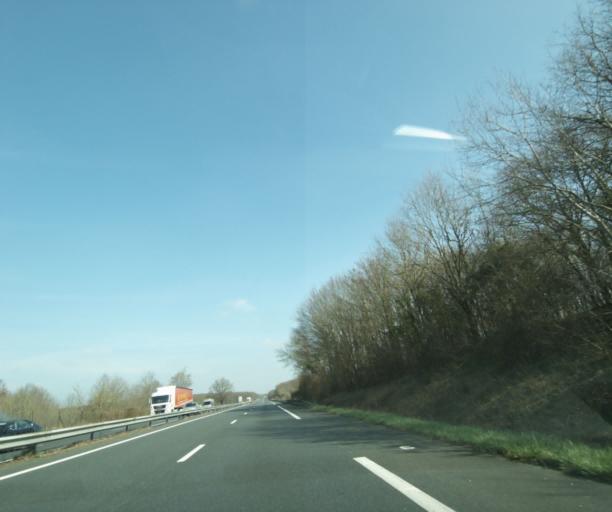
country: FR
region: Centre
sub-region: Departement de l'Indre
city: Saint-Marcel
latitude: 46.6110
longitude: 1.5189
